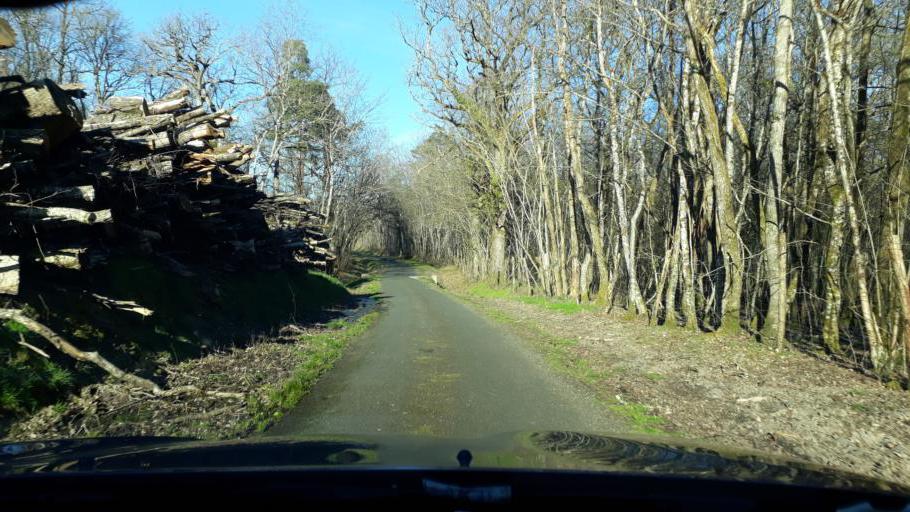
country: FR
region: Centre
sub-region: Departement du Loiret
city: Jouy-le-Potier
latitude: 47.7044
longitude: 1.8239
